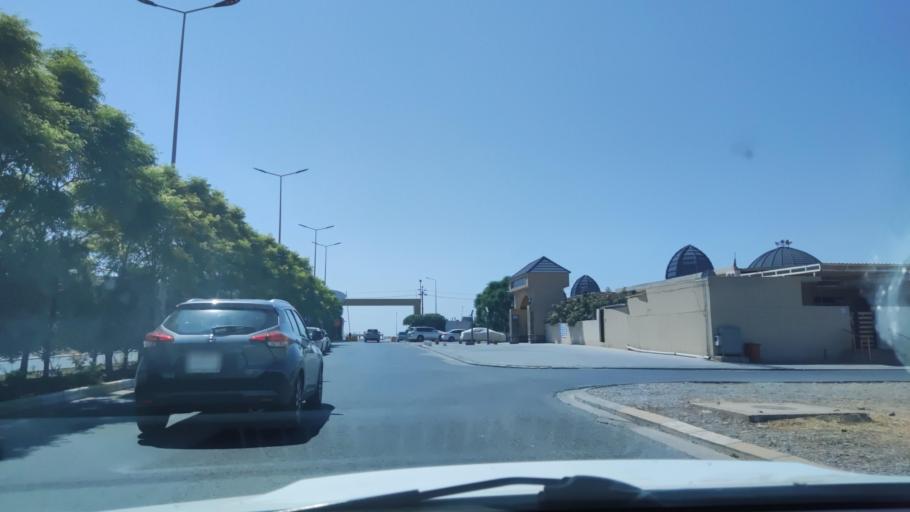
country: IQ
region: Arbil
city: Erbil
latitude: 36.2872
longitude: 44.0496
